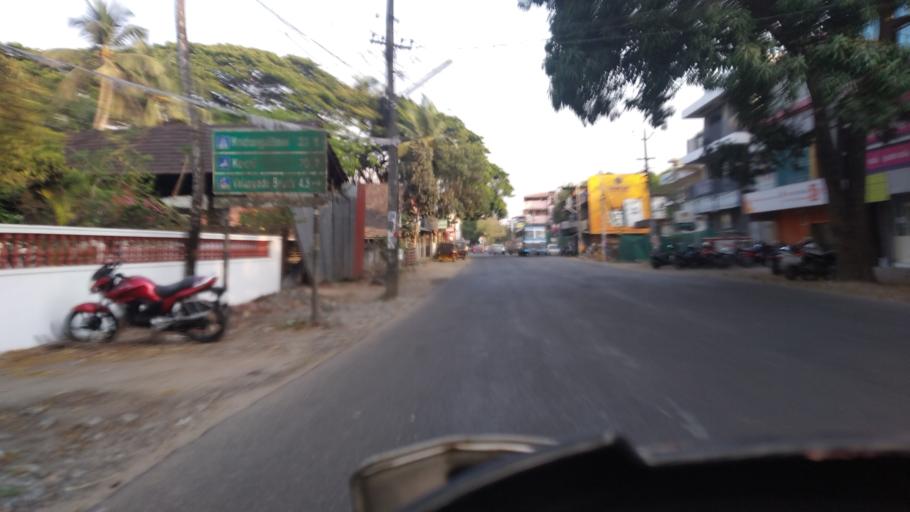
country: IN
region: Kerala
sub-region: Thrissur District
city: Thanniyam
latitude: 10.4053
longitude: 76.1112
